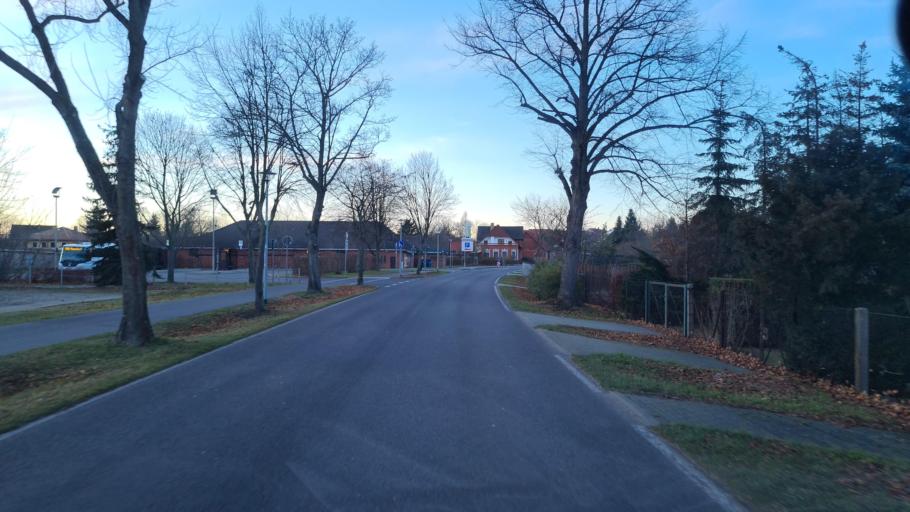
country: DE
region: Brandenburg
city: Vetschau
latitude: 51.7807
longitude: 14.0790
